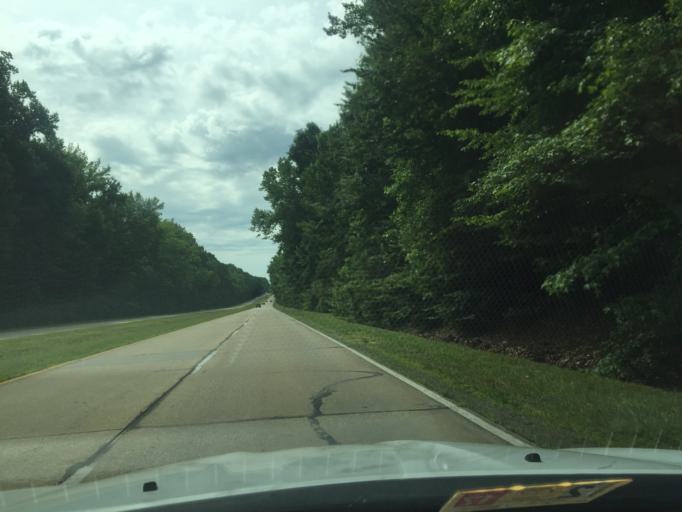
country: US
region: Virginia
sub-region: Charles City County
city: Charles City
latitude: 37.4694
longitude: -77.1130
